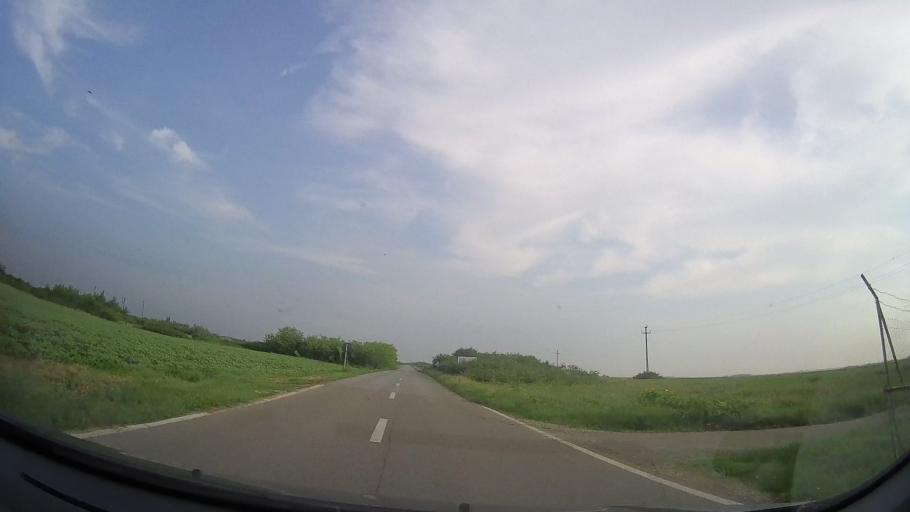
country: RS
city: Jasa Tomic
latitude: 45.4735
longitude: 20.8486
